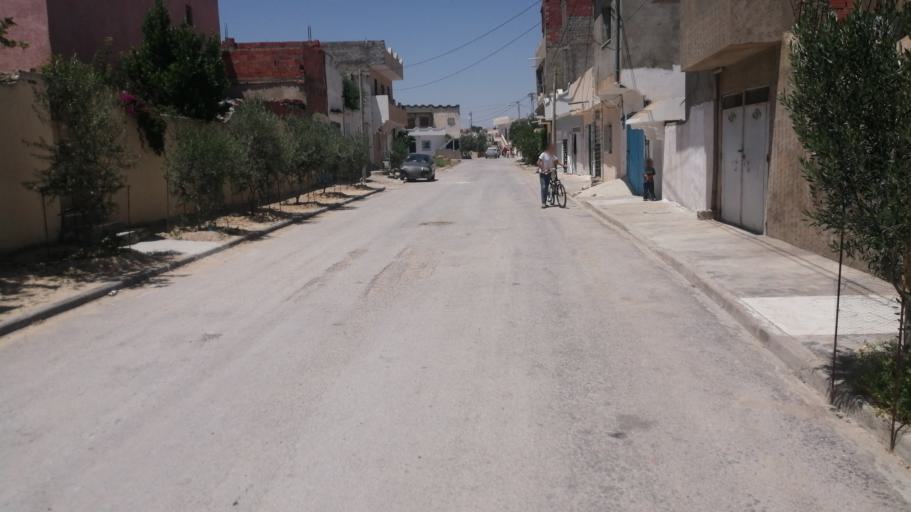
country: TN
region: Silyanah
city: Maktar
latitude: 35.8579
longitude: 9.2115
